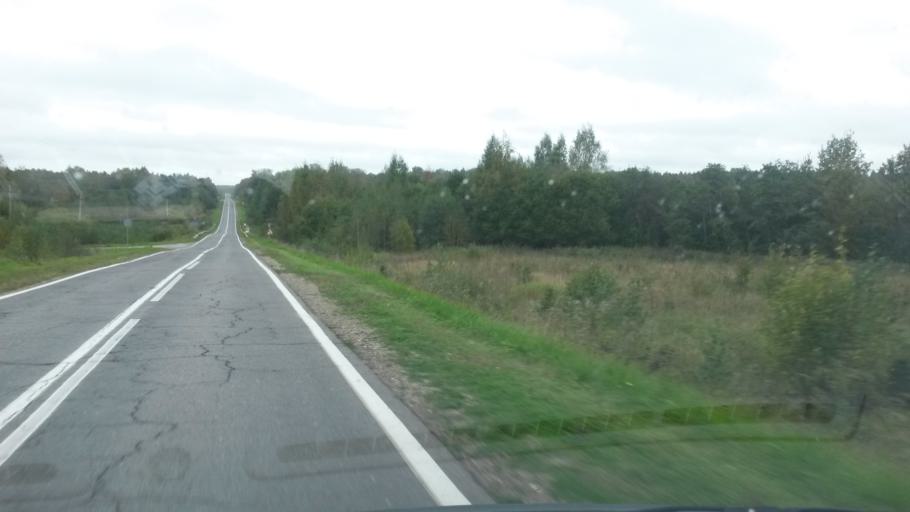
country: RU
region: Jaroslavl
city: Tutayev
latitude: 57.9512
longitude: 39.4270
